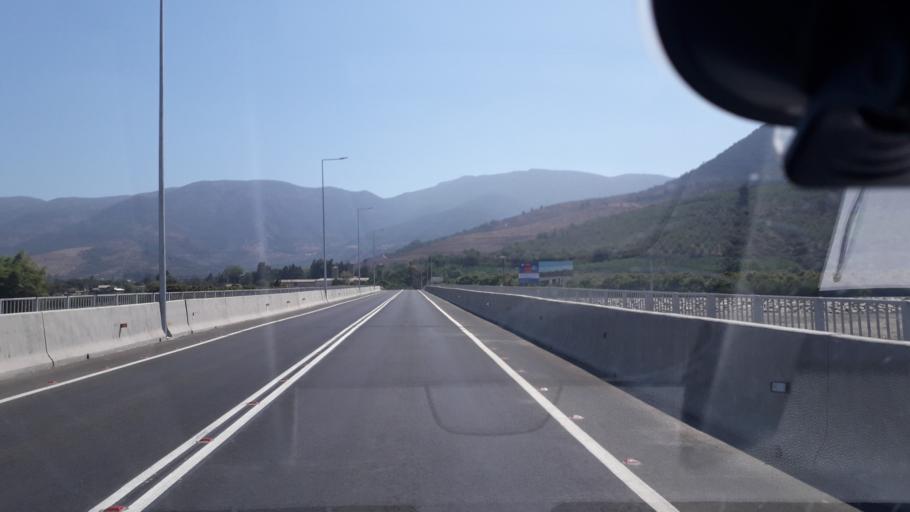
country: CL
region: Valparaiso
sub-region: Provincia de Quillota
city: Hacienda La Calera
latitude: -32.8164
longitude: -71.2436
